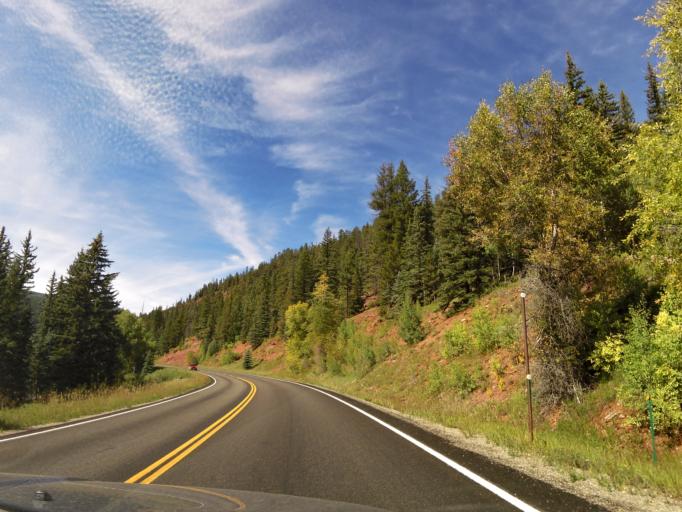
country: US
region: Colorado
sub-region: Montezuma County
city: Mancos
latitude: 37.6005
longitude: -108.1152
